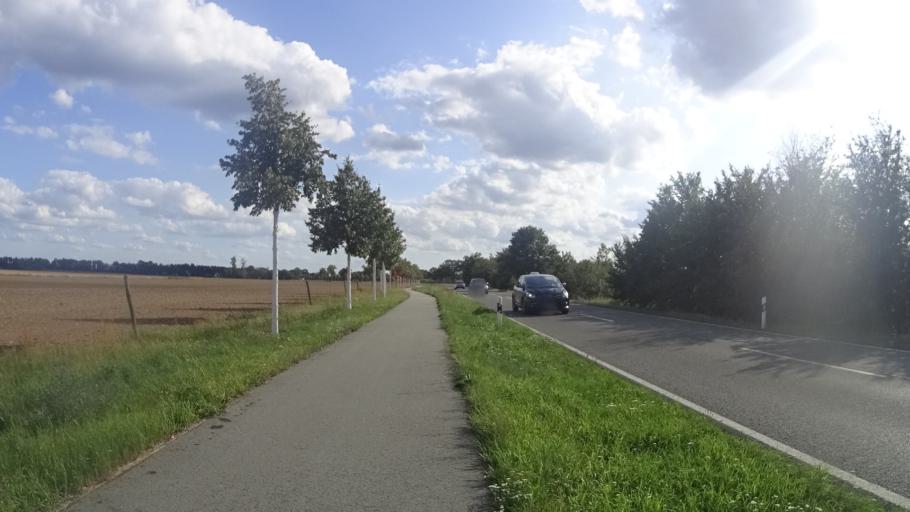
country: DE
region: Brandenburg
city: Rathenow
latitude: 52.6424
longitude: 12.3303
